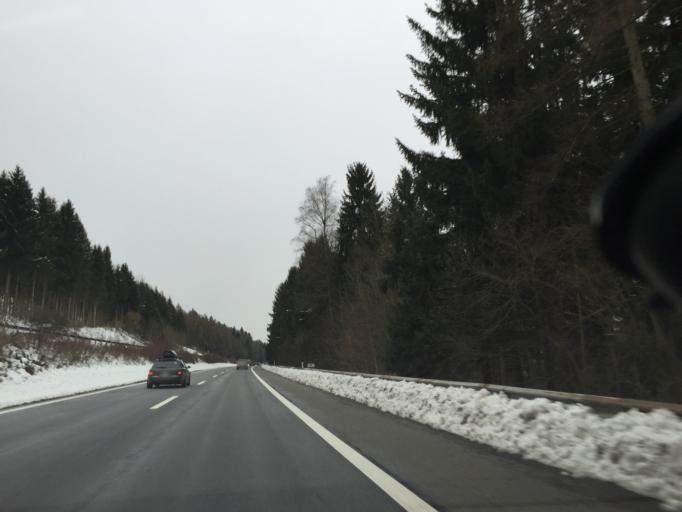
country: CH
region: Zurich
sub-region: Bezirk Horgen
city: Horgen / Scheller-Stockerstrasse
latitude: 47.2578
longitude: 8.5834
